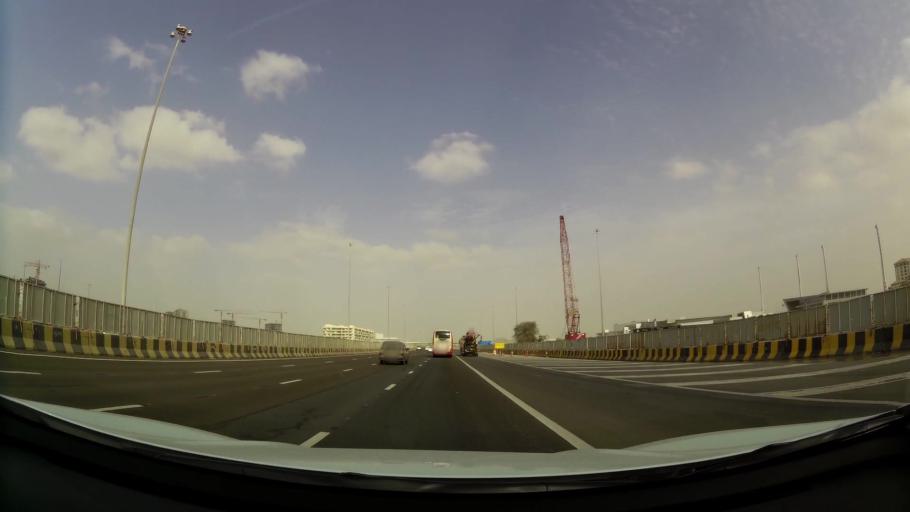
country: AE
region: Abu Dhabi
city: Abu Dhabi
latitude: 24.4469
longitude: 54.6073
